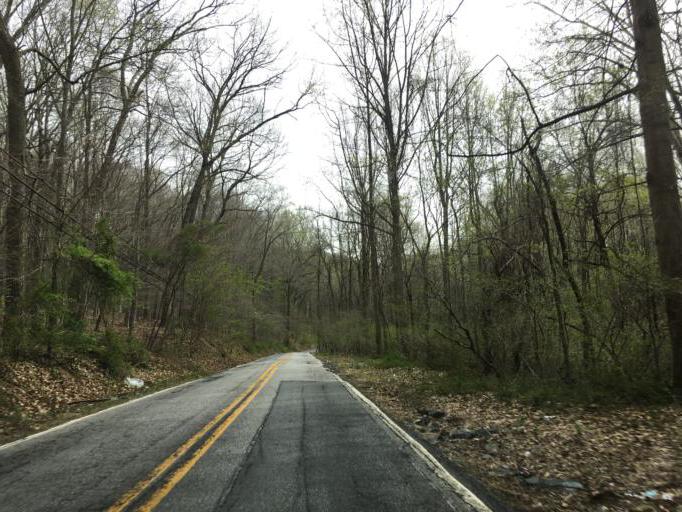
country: US
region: Maryland
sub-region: Baltimore County
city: Hunt Valley
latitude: 39.5257
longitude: -76.6143
